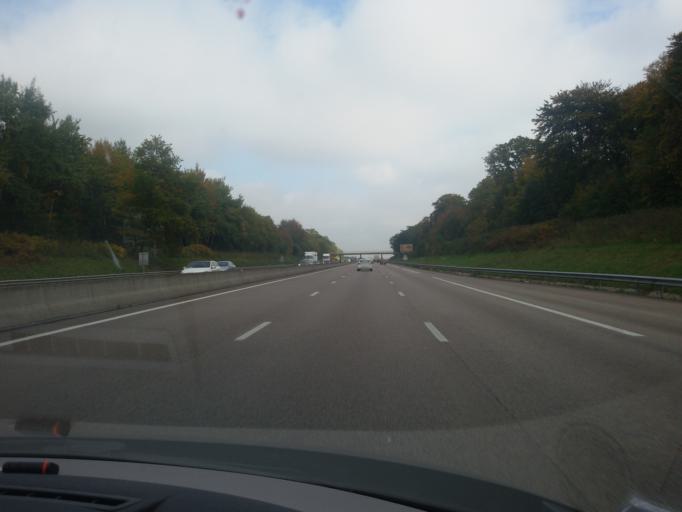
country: FR
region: Haute-Normandie
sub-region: Departement de la Seine-Maritime
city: Grand-Couronne
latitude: 49.3417
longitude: 1.0297
